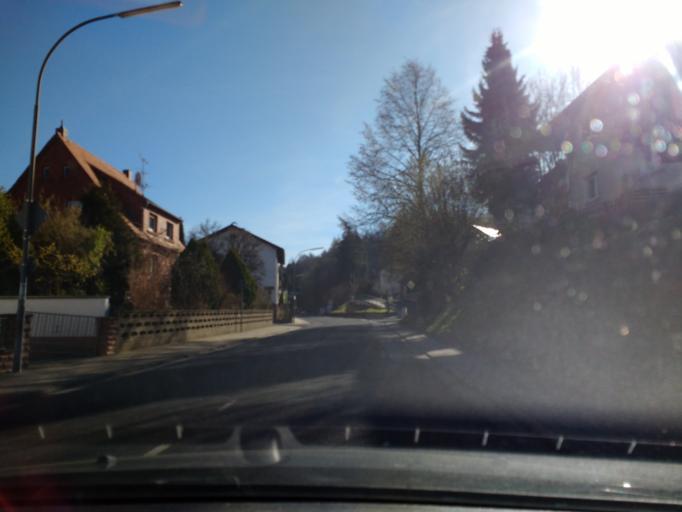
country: DE
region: Bavaria
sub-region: Regierungsbezirk Unterfranken
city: Geiselbach
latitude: 50.1387
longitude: 9.1611
